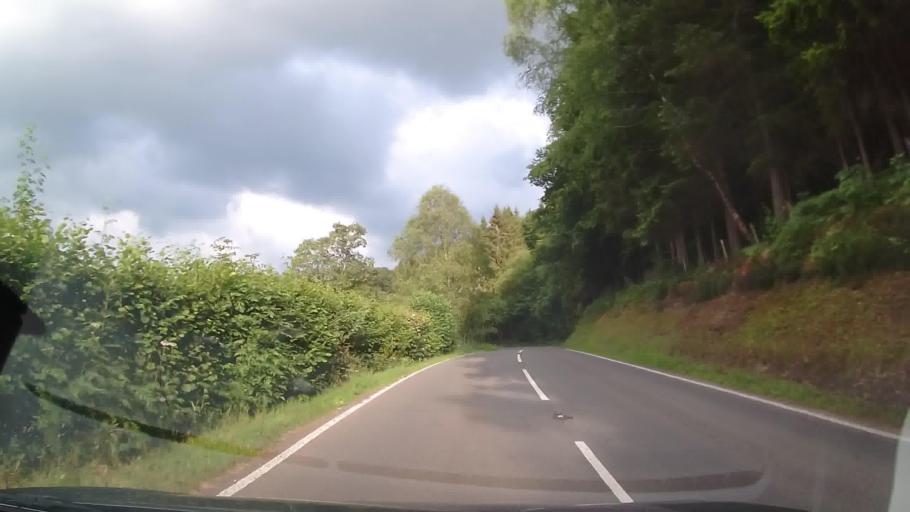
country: GB
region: Wales
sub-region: Gwynedd
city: Bala
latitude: 52.9055
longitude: -3.5298
